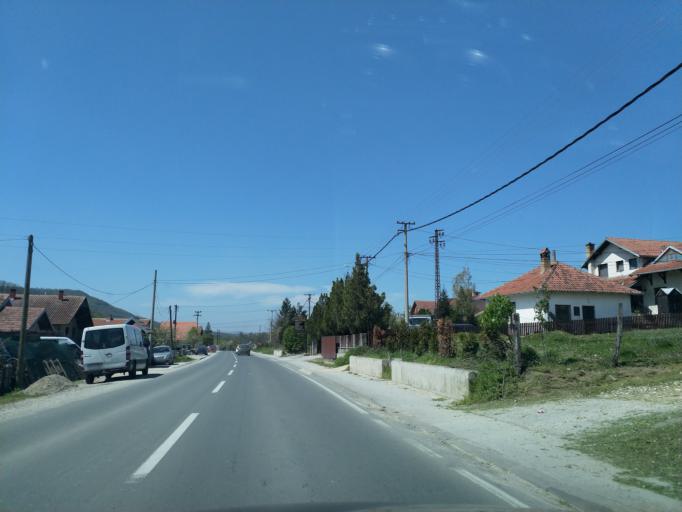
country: RS
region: Central Serbia
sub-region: Sumadijski Okrug
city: Arangelovac
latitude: 44.3249
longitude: 20.5306
